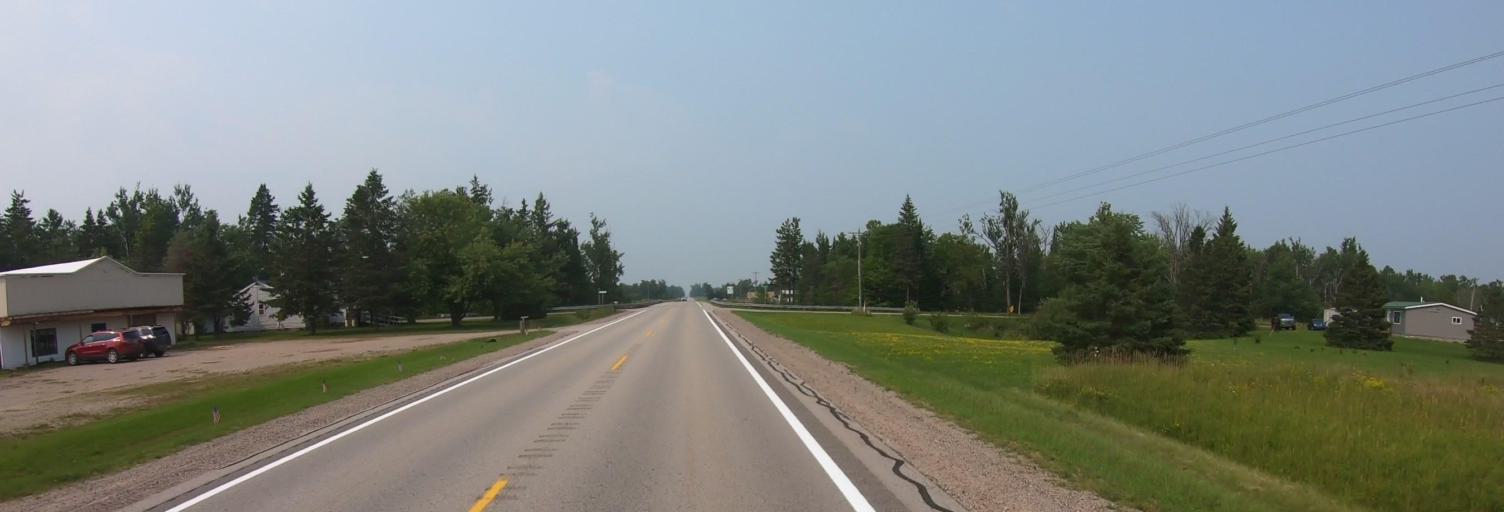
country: US
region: Michigan
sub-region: Chippewa County
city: Sault Ste. Marie
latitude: 46.2293
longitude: -84.3634
